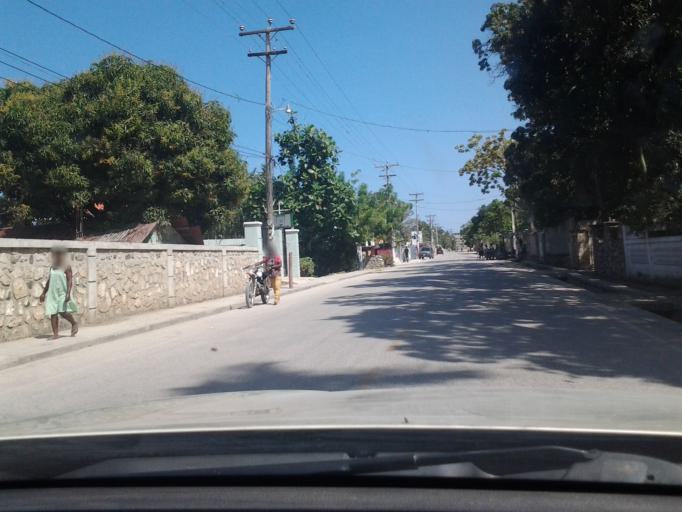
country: HT
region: Ouest
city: Tigwav
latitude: 18.4378
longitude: -72.8558
